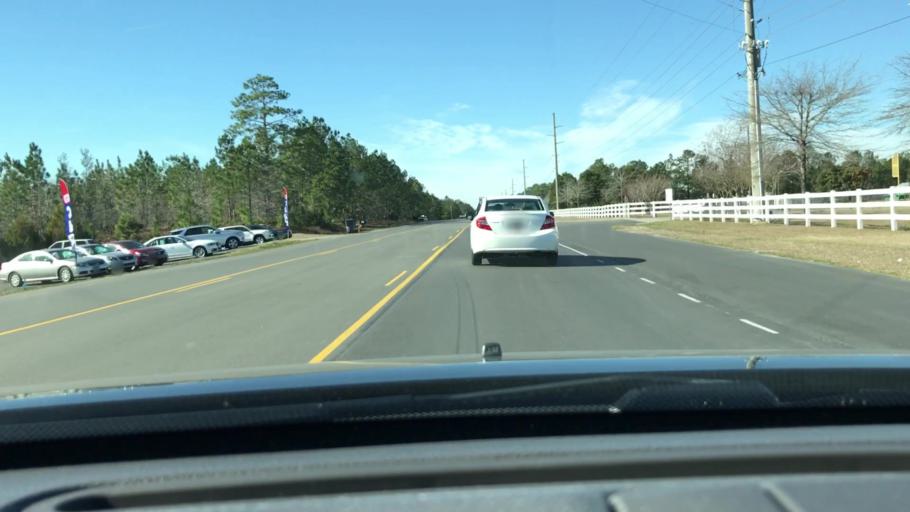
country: US
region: North Carolina
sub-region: Brunswick County
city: Shallotte
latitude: 33.9793
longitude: -78.4110
